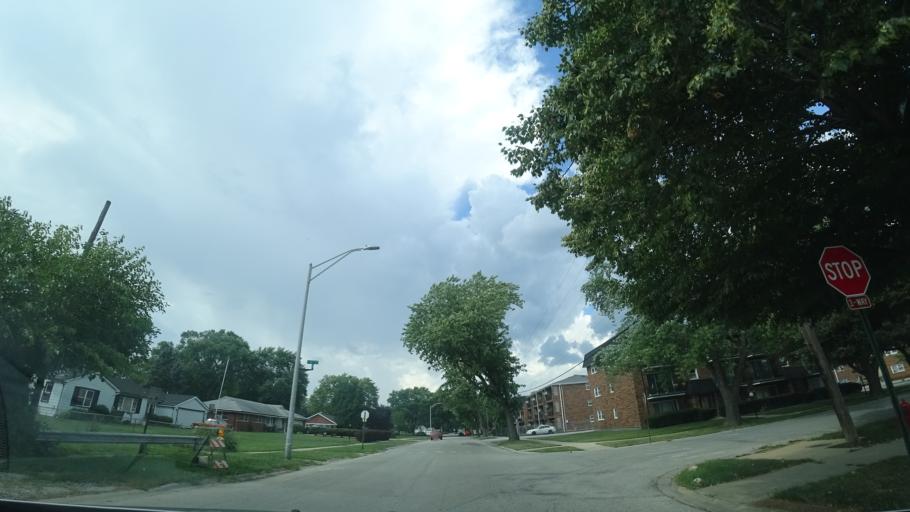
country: US
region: Illinois
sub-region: Cook County
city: Merrionette Park
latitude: 41.6748
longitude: -87.7149
